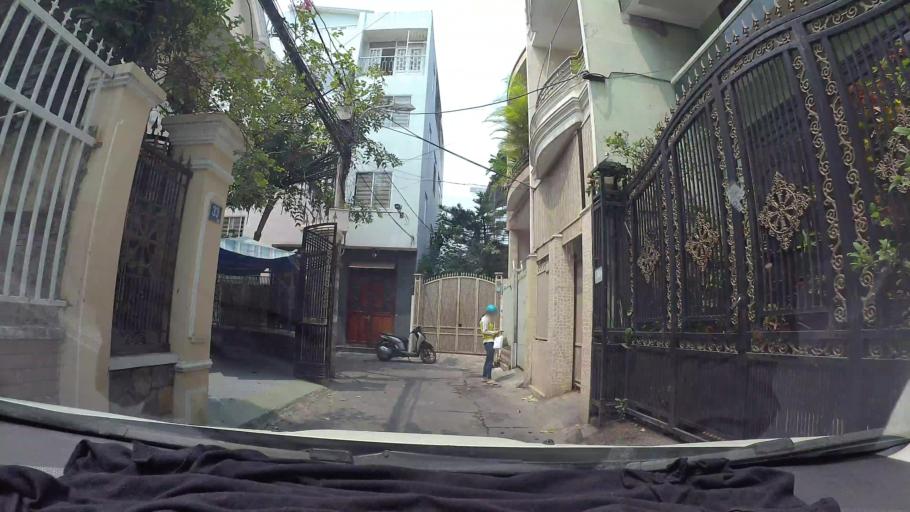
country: VN
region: Da Nang
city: Da Nang
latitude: 16.0825
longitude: 108.2189
